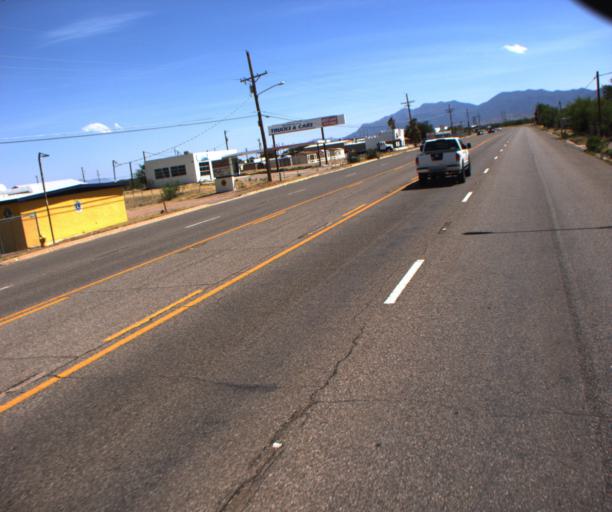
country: US
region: Arizona
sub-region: Cochise County
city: Huachuca City
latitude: 31.6234
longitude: -110.3357
